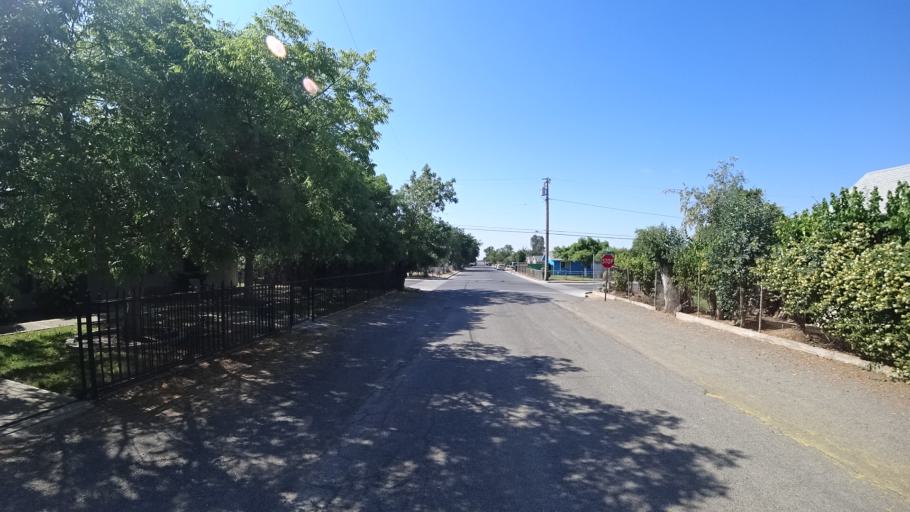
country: US
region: California
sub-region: Kings County
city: Home Garden
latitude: 36.3044
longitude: -119.6354
